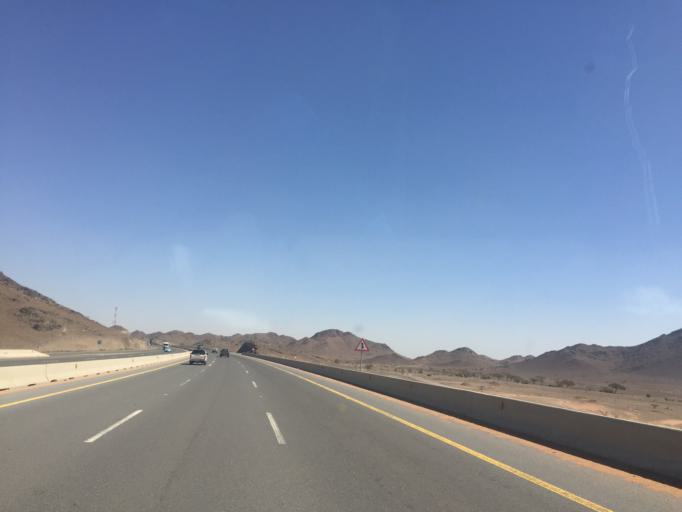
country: SA
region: Al Madinah al Munawwarah
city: Sultanah
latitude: 24.3015
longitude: 39.3943
